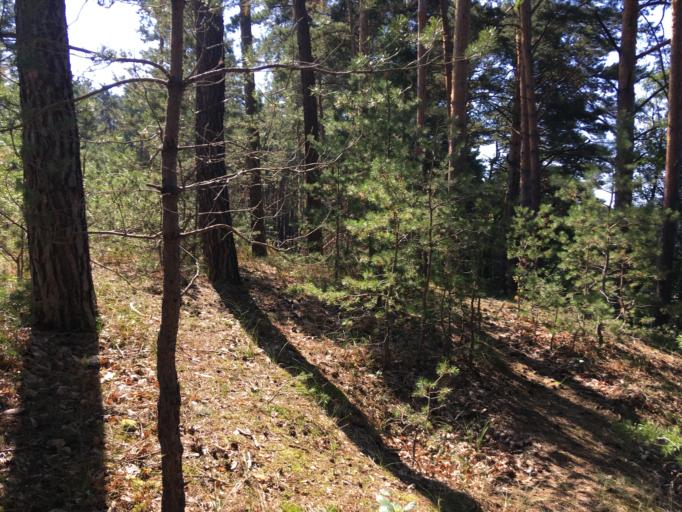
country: DE
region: Brandenburg
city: Gross Koris
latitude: 52.2056
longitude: 13.7458
